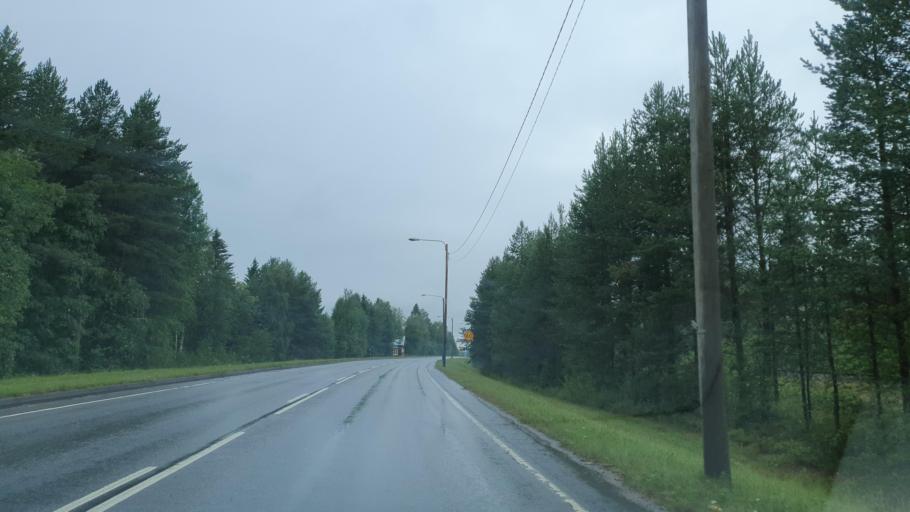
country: FI
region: Lapland
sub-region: Itae-Lappi
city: Kemijaervi
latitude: 66.7135
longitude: 27.4911
